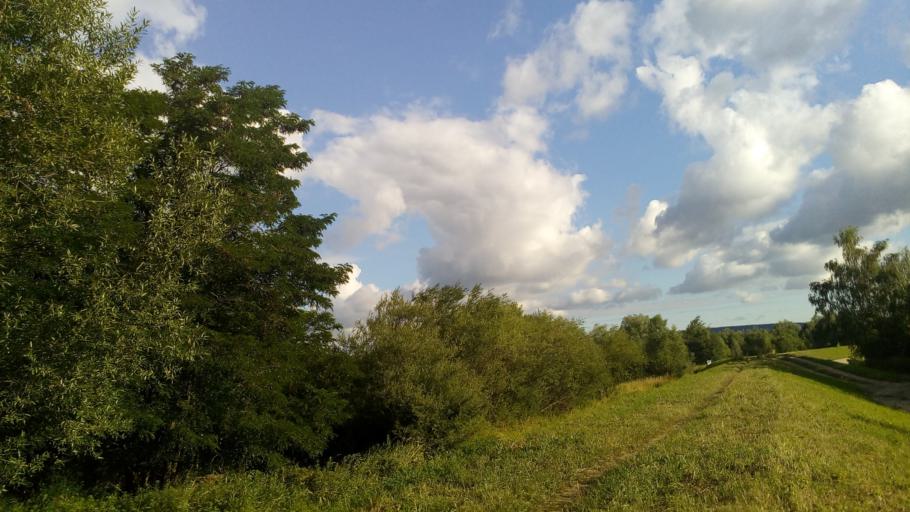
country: PL
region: Lesser Poland Voivodeship
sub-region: Powiat nowosadecki
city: Stary Sacz
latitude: 49.5806
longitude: 20.6536
